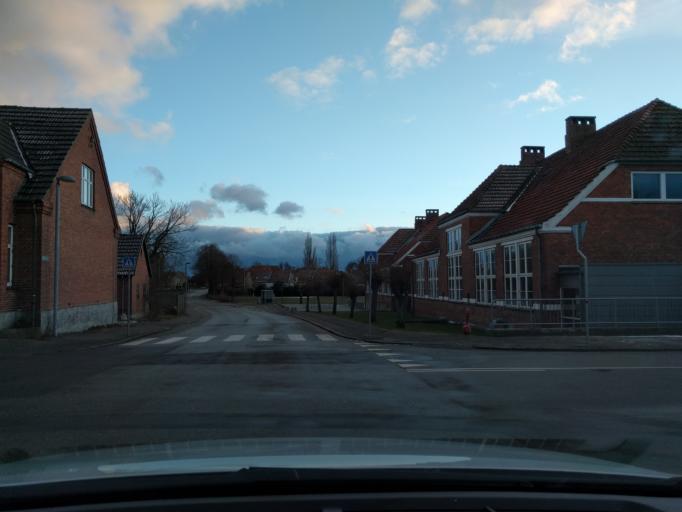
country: DK
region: Zealand
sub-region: Guldborgsund Kommune
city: Stubbekobing
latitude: 54.8895
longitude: 12.0383
